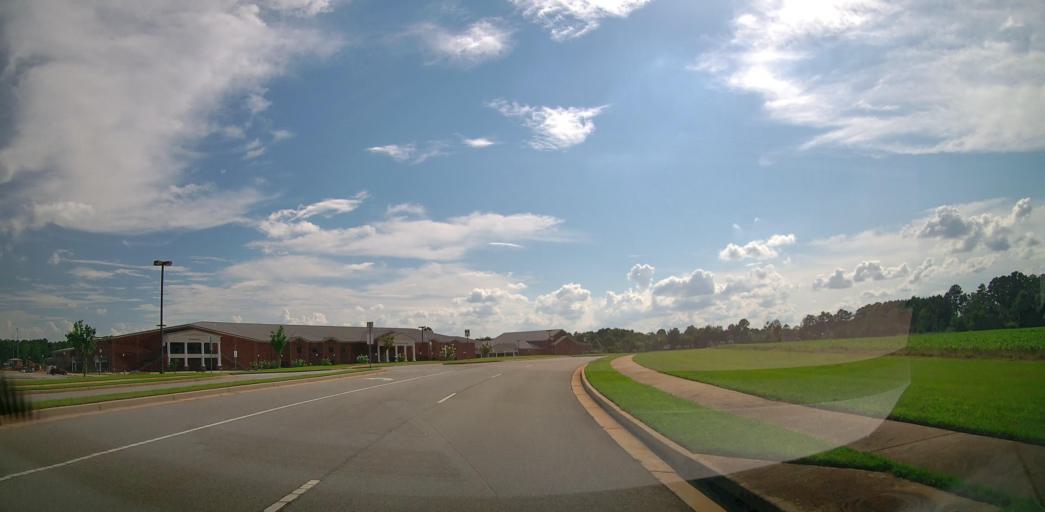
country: US
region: Georgia
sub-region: Houston County
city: Robins Air Force Base
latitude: 32.5158
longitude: -83.6109
